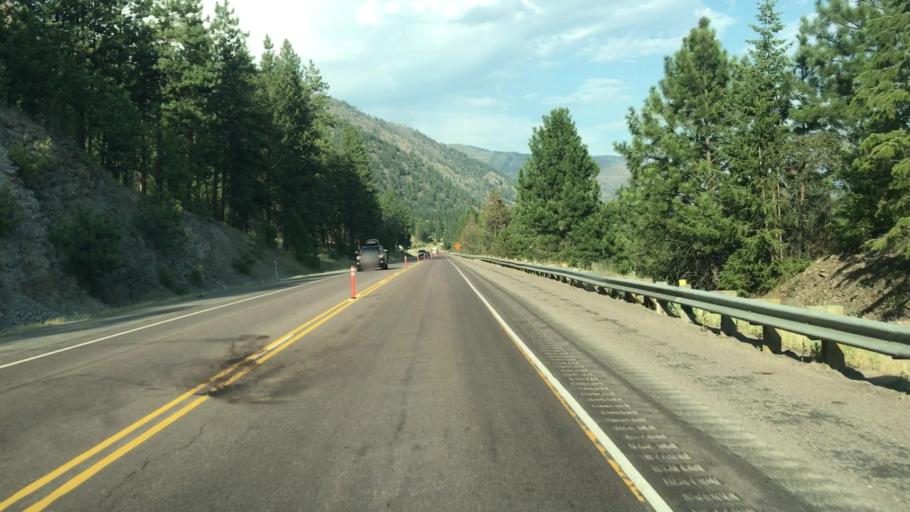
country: US
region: Montana
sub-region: Mineral County
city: Superior
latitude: 47.0169
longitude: -114.6869
